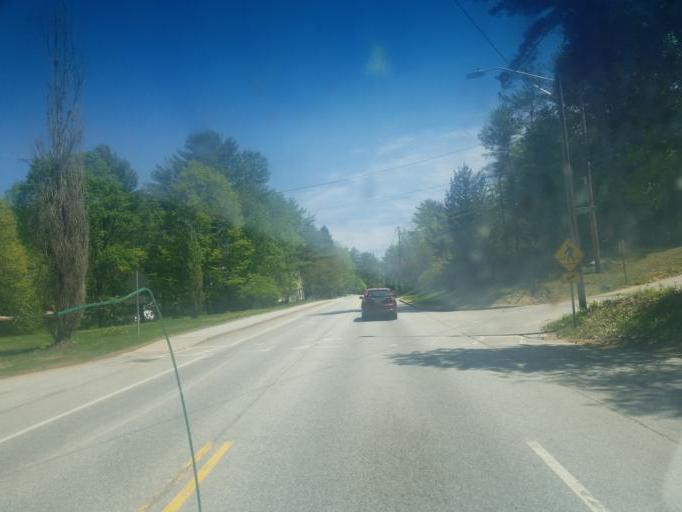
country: US
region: New Hampshire
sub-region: Grafton County
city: Plymouth
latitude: 43.7642
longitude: -71.7113
